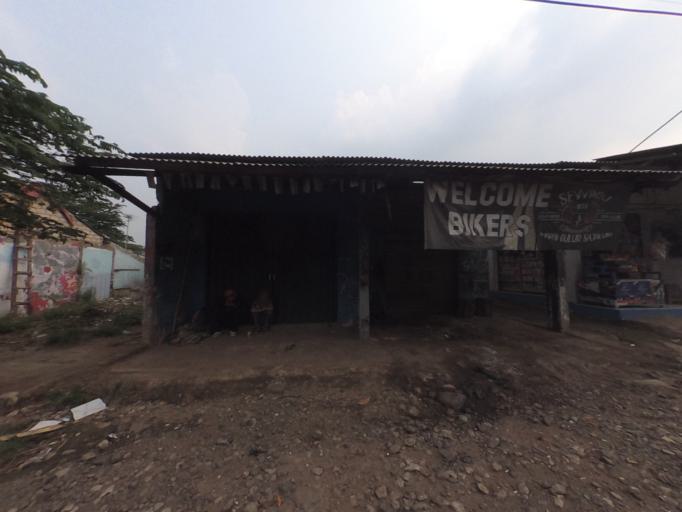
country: ID
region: West Java
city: Ciampea
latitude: -6.5625
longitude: 106.6843
